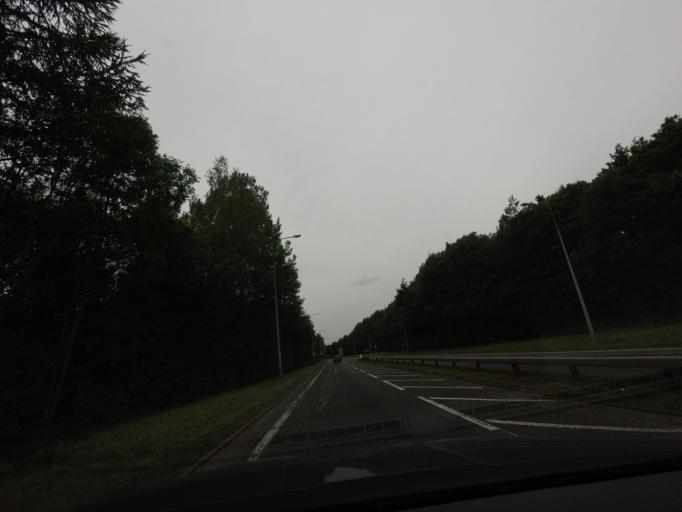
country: GB
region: England
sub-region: Telford and Wrekin
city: Madeley
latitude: 52.6457
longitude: -2.4433
